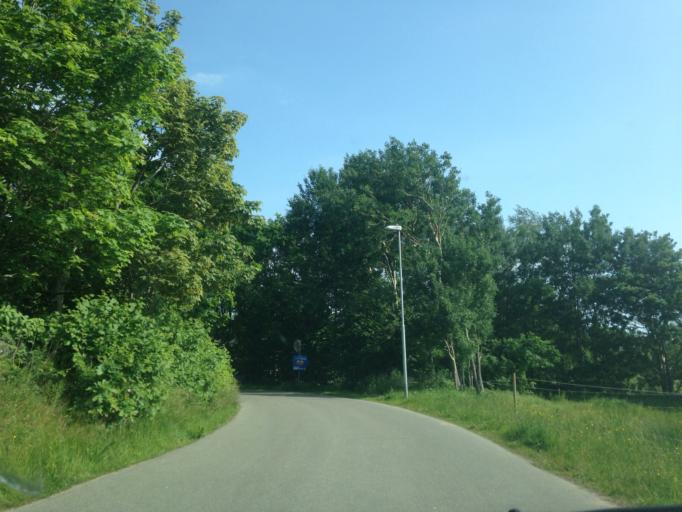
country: SE
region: Vaestra Goetaland
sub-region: Goteborg
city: Torslanda
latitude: 57.7741
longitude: 11.8344
